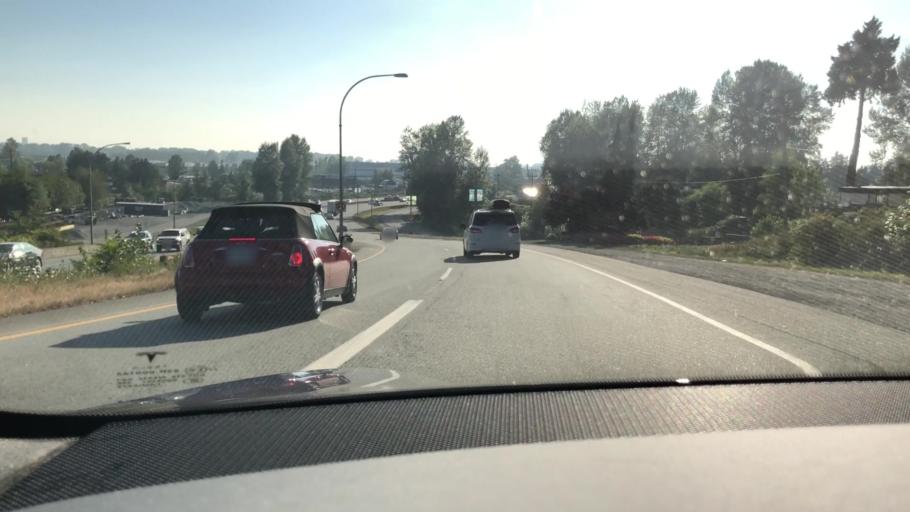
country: CA
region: British Columbia
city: New Westminster
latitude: 49.1969
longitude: -122.9547
